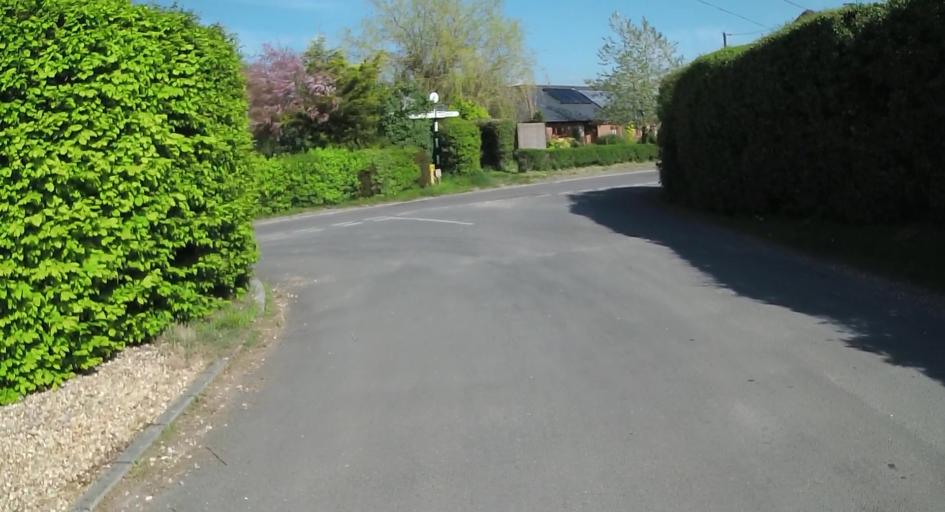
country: GB
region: England
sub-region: Hampshire
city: Kings Worthy
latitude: 51.1525
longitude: -1.2723
